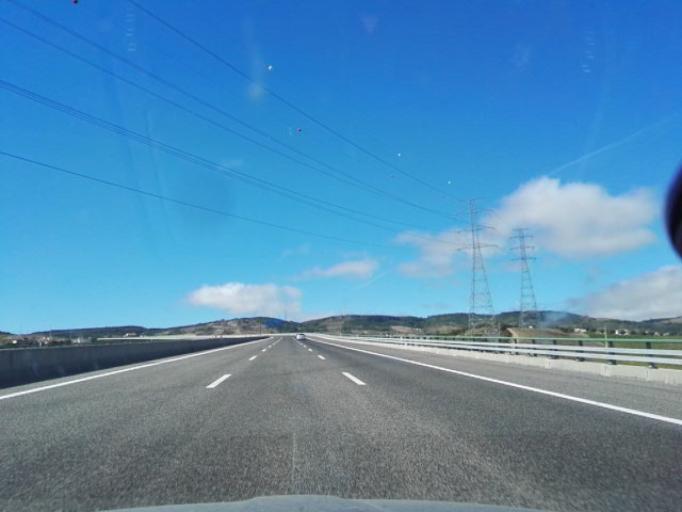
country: PT
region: Lisbon
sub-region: Arruda Dos Vinhos
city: Arruda dos Vinhos
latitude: 38.9810
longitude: -9.0558
